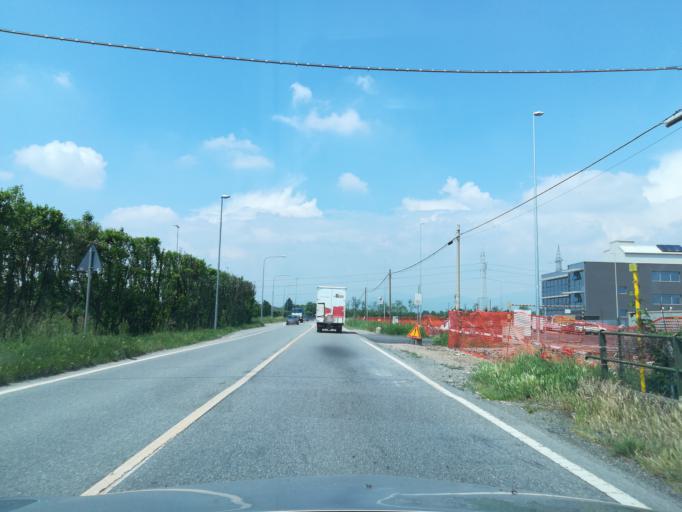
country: IT
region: Lombardy
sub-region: Provincia di Bergamo
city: Cavernago
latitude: 45.6380
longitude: 9.7569
